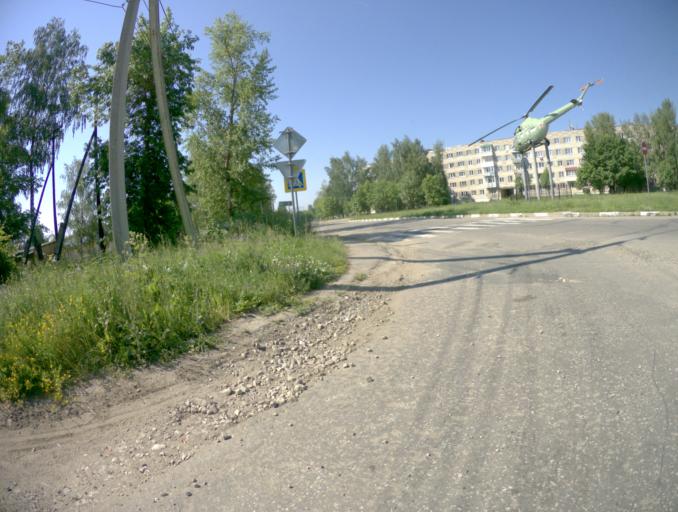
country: RU
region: Vladimir
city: Novovyazniki
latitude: 56.2313
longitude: 42.1984
